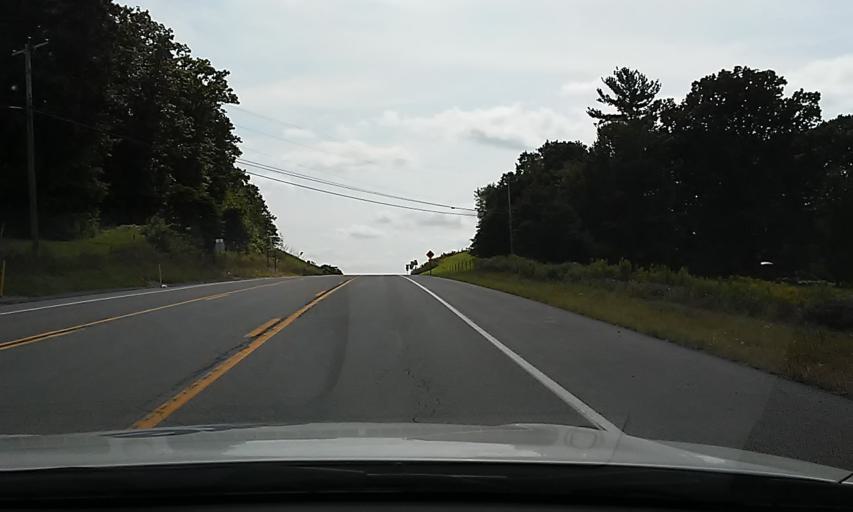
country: US
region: Pennsylvania
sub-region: Jefferson County
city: Punxsutawney
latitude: 40.9213
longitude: -78.9857
